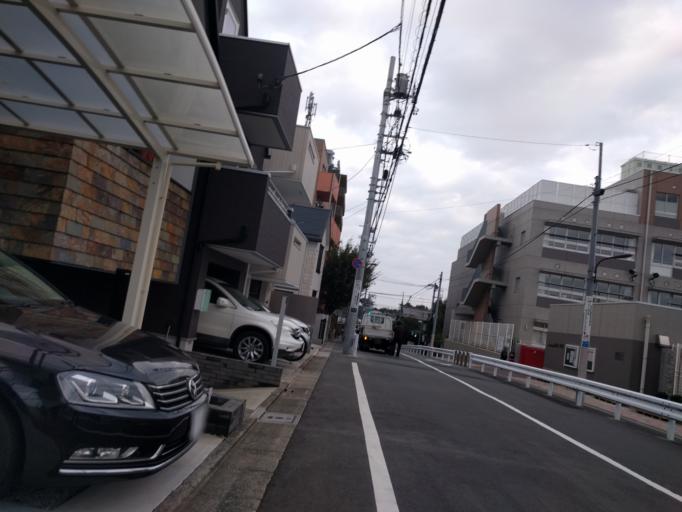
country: JP
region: Tokyo
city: Tokyo
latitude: 35.6426
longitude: 139.6448
